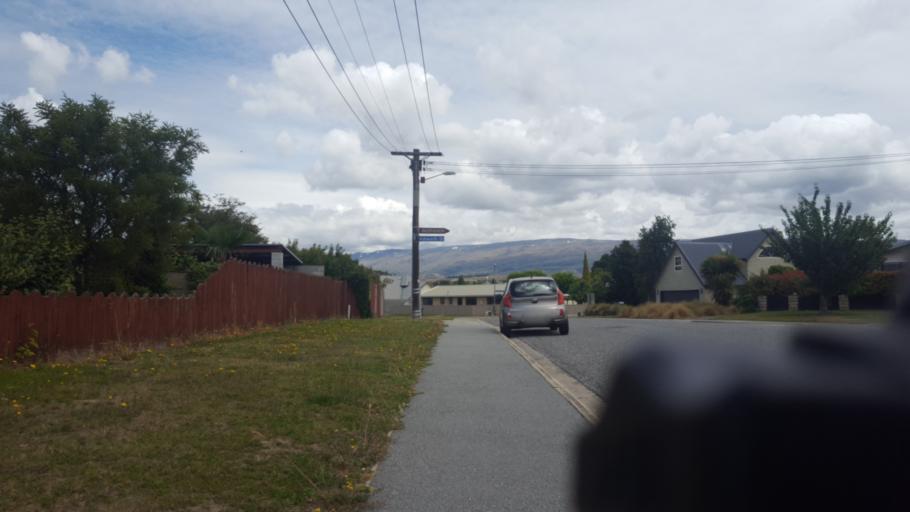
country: NZ
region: Otago
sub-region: Queenstown-Lakes District
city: Wanaka
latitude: -45.2513
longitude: 169.3839
